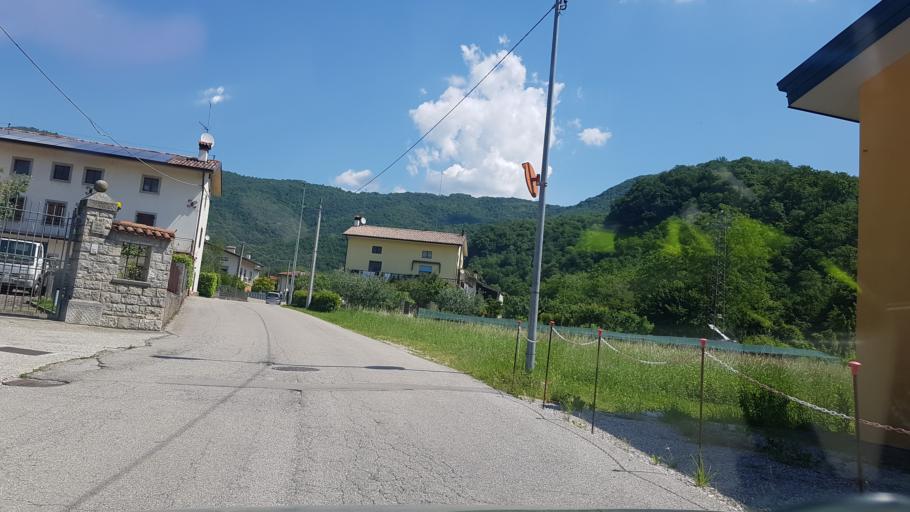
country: IT
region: Friuli Venezia Giulia
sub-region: Provincia di Udine
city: Torreano
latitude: 46.1329
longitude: 13.4356
